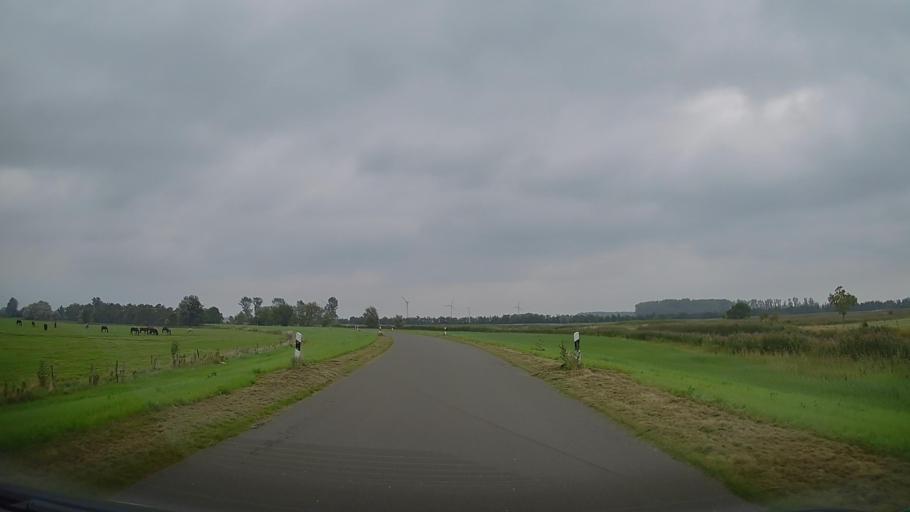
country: DE
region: Lower Saxony
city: Neuhaus an der Oste
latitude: 53.8082
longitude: 9.0377
